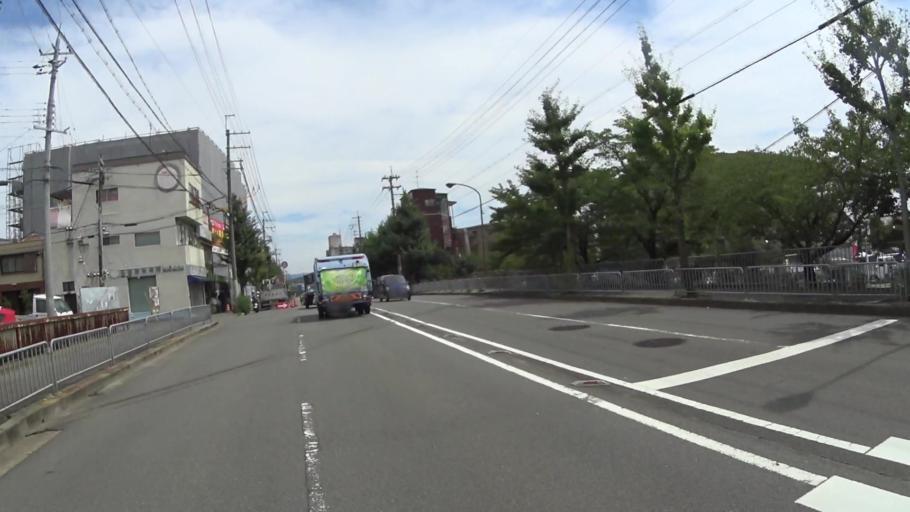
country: JP
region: Kyoto
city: Muko
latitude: 35.0208
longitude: 135.6837
